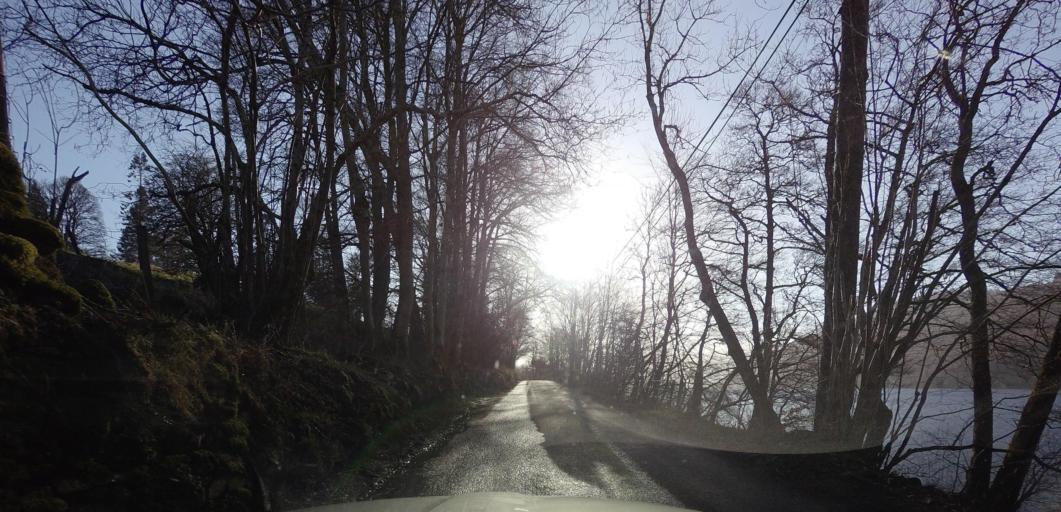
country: GB
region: Scotland
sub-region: Perth and Kinross
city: Aberfeldy
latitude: 56.5813
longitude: -3.9982
